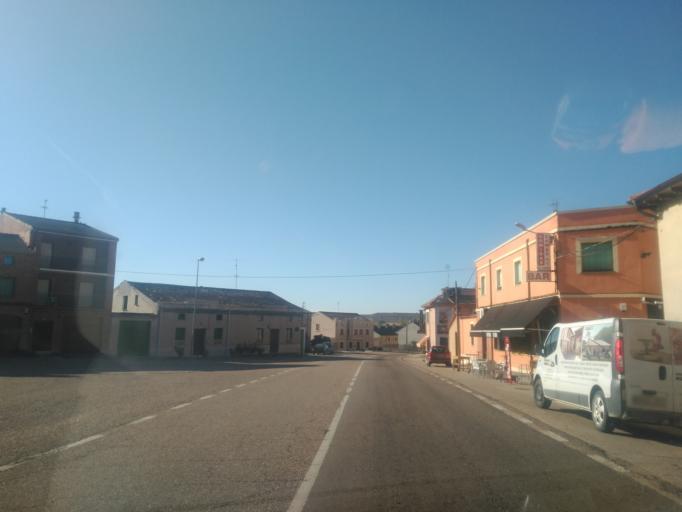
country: ES
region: Castille and Leon
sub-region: Provincia de Burgos
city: Castrillo de la Vega
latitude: 41.6519
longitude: -3.7788
